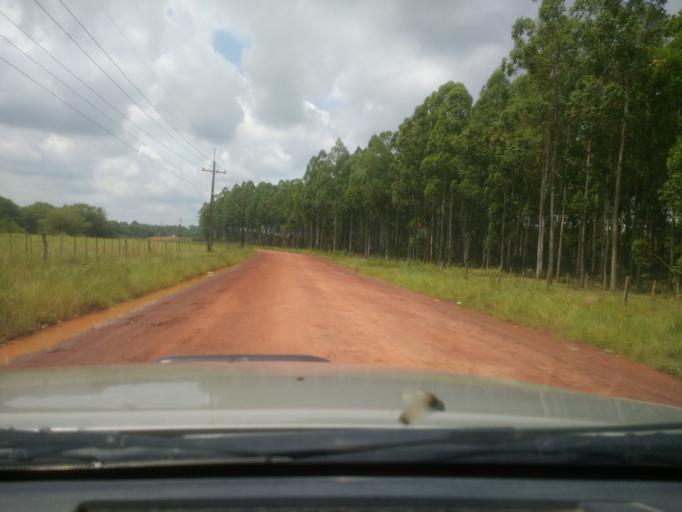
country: PY
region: San Pedro
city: Puerto Rosario
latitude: -24.4028
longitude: -57.1041
